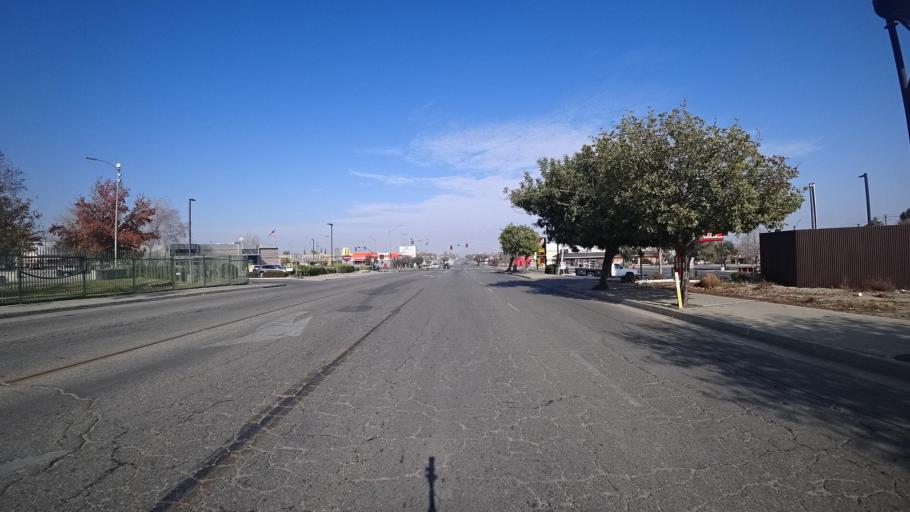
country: US
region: California
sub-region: Kern County
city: Taft
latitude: 35.1440
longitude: -119.4651
